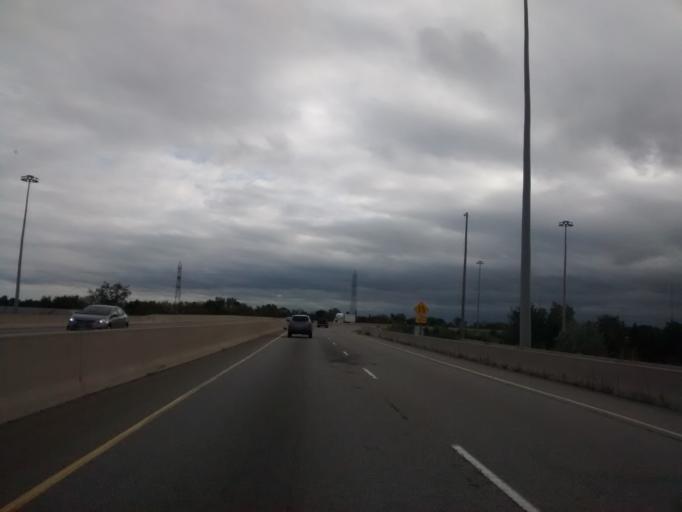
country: CA
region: Ontario
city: Hamilton
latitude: 43.2481
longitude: -79.7627
